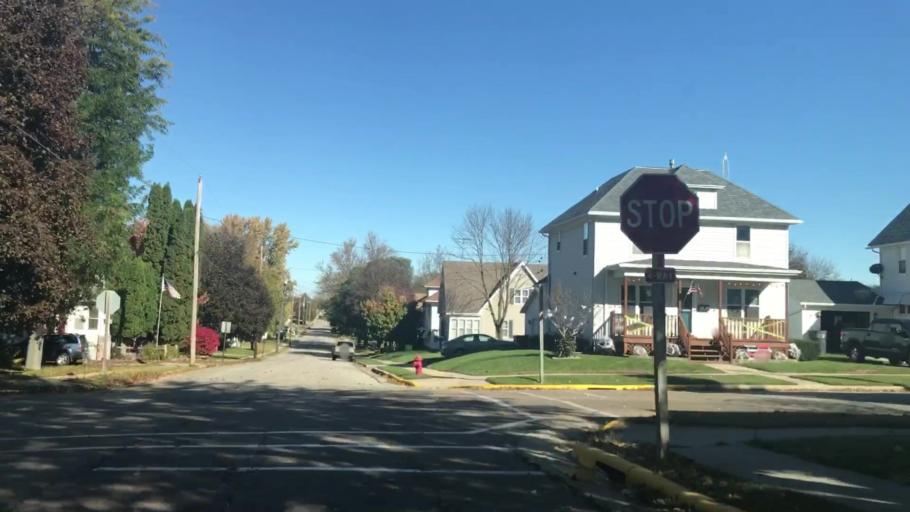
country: US
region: Wisconsin
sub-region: Dodge County
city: Mayville
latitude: 43.4974
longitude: -88.5525
